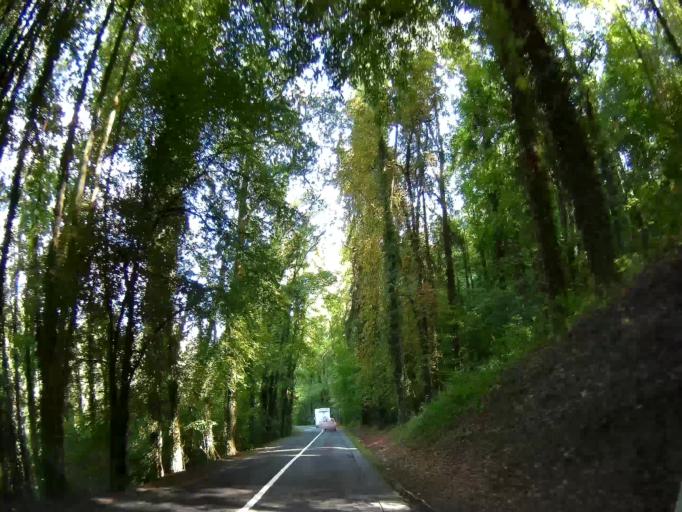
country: BE
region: Wallonia
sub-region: Province de Namur
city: Onhaye
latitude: 50.3062
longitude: 4.7656
